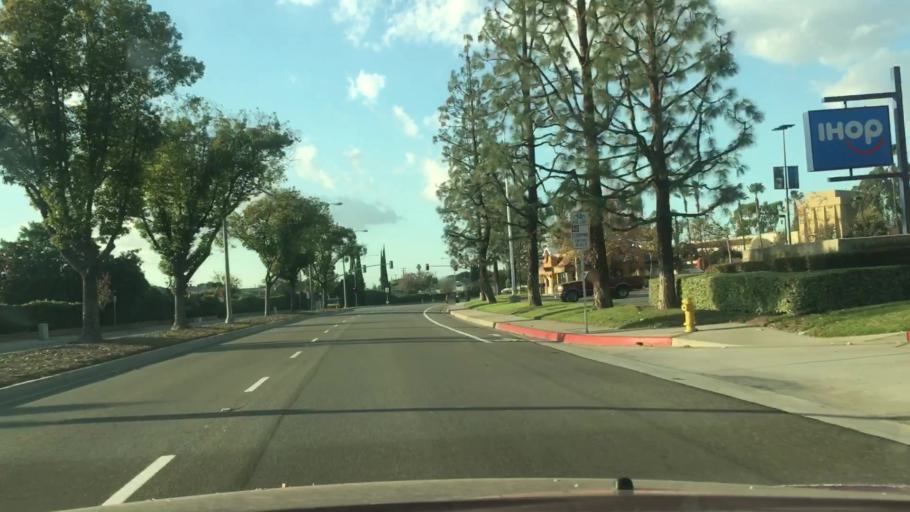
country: US
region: California
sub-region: Los Angeles County
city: La Mirada
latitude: 33.8944
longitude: -118.0079
